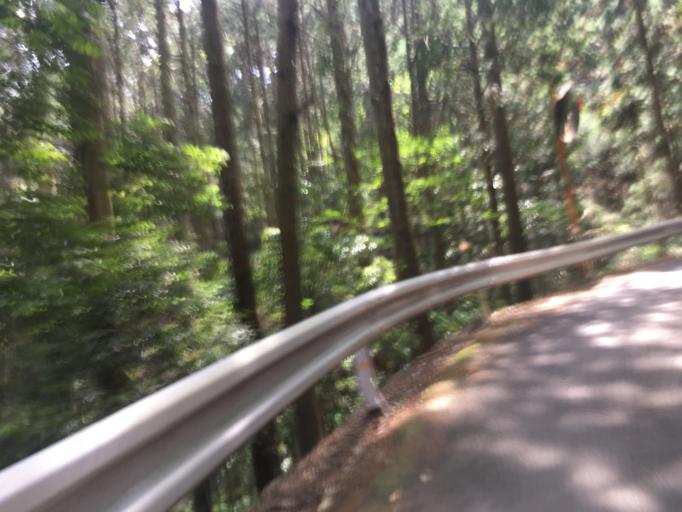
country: JP
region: Kyoto
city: Muko
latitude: 35.0296
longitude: 135.6578
